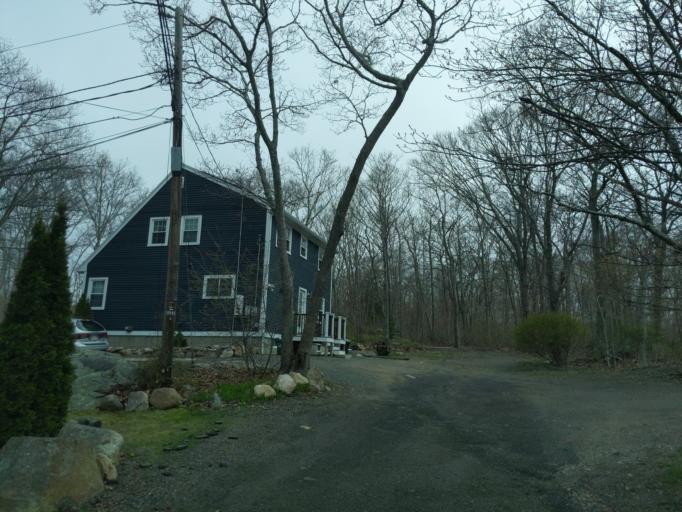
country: US
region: Massachusetts
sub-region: Essex County
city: Rockport
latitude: 42.6378
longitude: -70.6089
